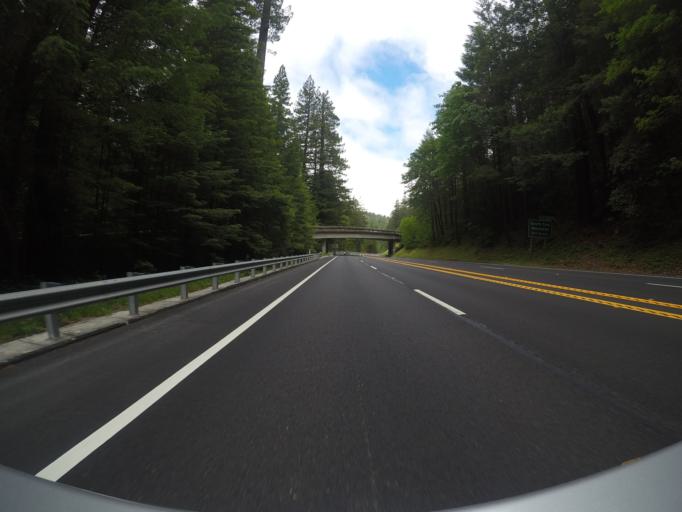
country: US
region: California
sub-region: Humboldt County
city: Rio Dell
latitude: 40.3441
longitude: -123.9318
